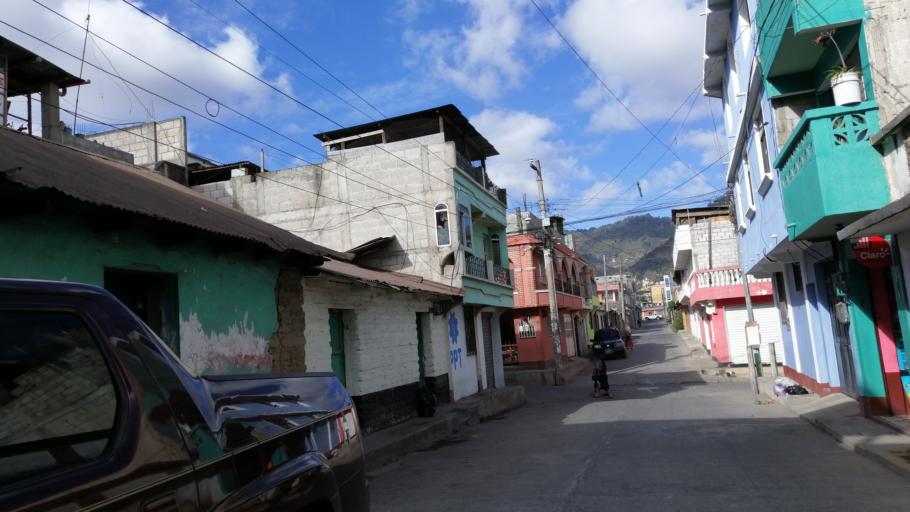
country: GT
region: Quetzaltenango
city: Ostuncalco
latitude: 14.8669
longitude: -91.6227
